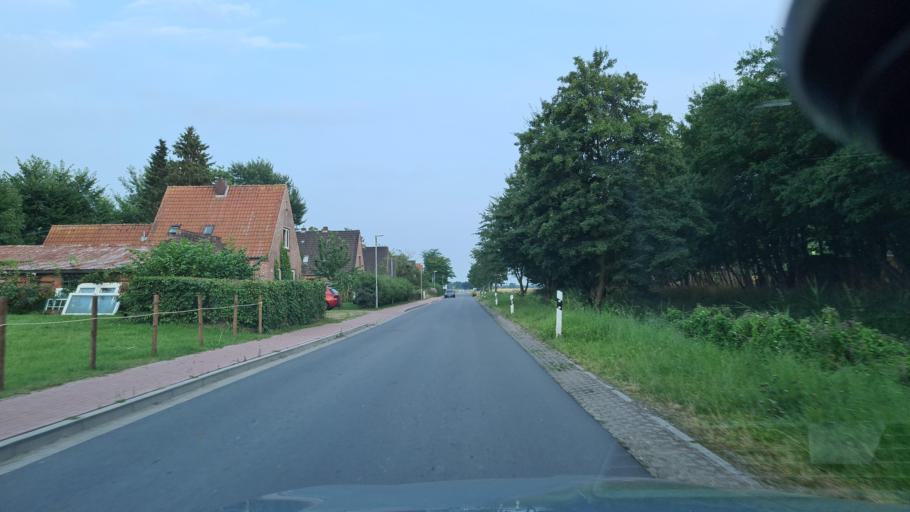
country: DE
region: Schleswig-Holstein
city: Oldenswort
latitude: 54.3700
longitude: 8.9443
